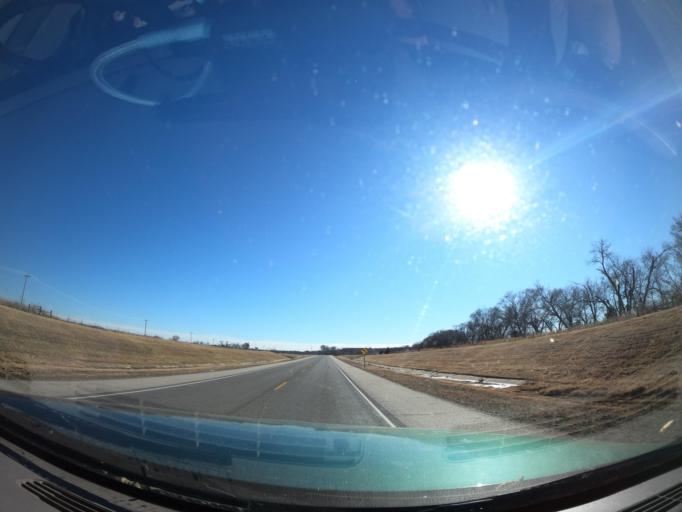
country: US
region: Oklahoma
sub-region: Muskogee County
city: Haskell
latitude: 35.7932
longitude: -95.6681
